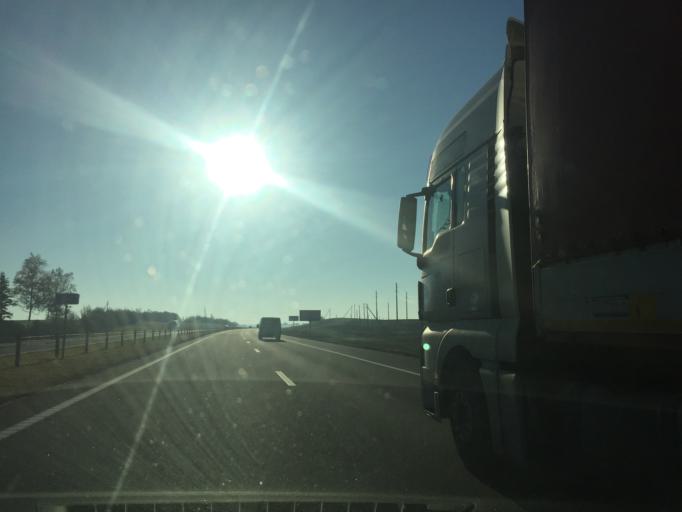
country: BY
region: Minsk
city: Luhavaya Slabada
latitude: 53.7769
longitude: 27.8514
